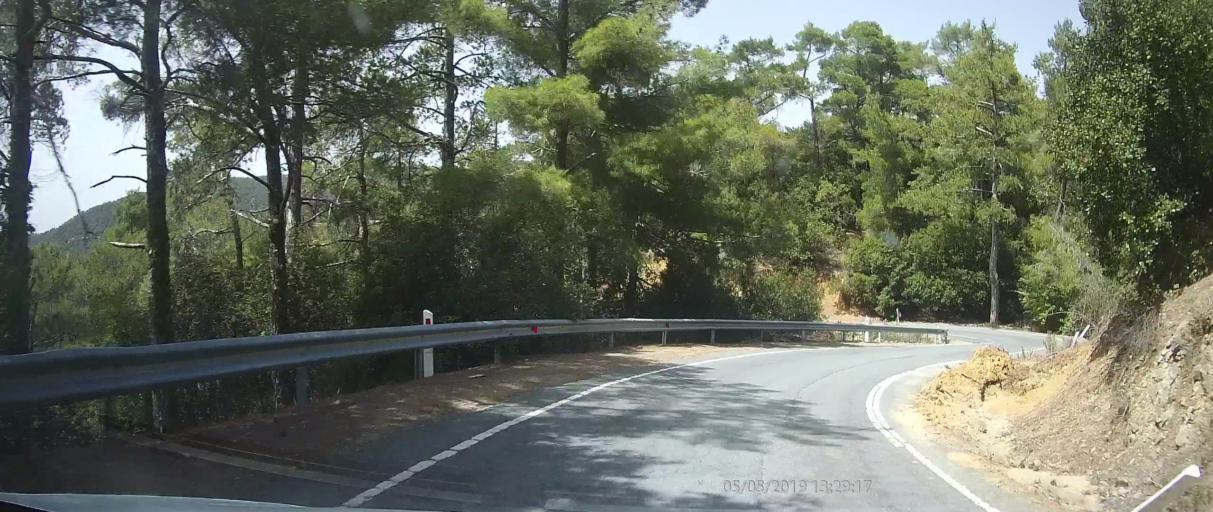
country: CY
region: Lefkosia
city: Kakopetria
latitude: 34.8985
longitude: 32.8500
